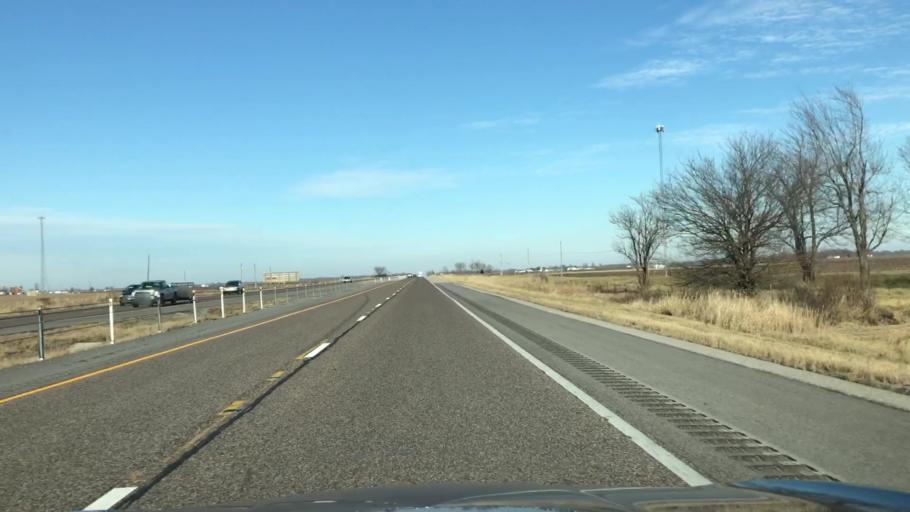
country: US
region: Illinois
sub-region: Madison County
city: Edwardsville
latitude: 38.8324
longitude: -89.8778
